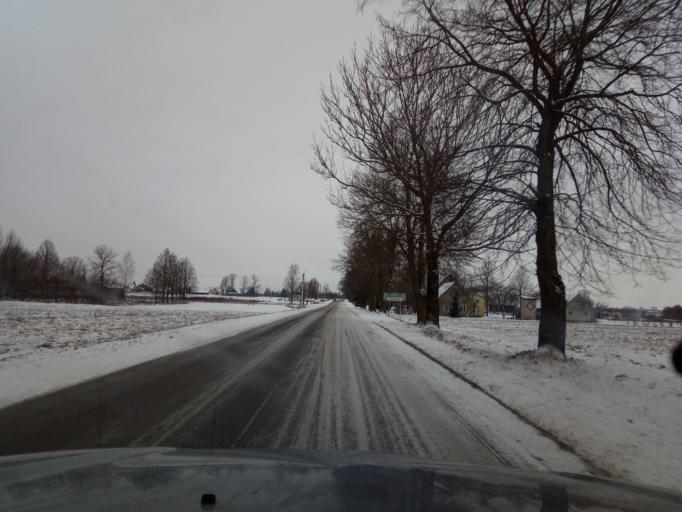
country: LT
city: Ramygala
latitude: 55.4925
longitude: 24.4954
